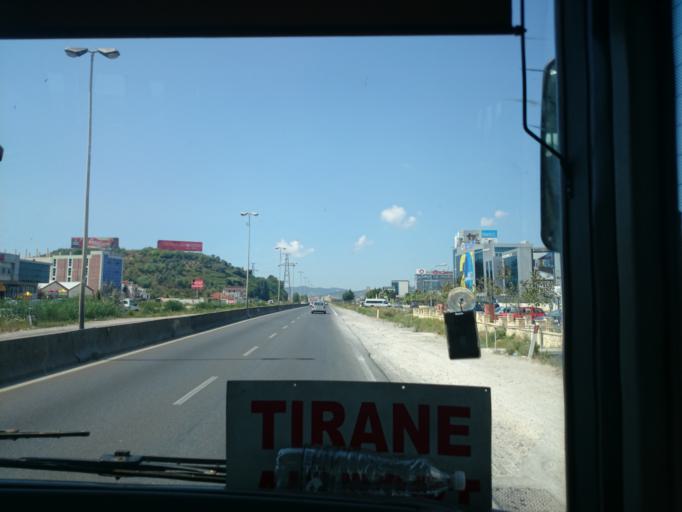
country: AL
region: Tirane
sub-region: Rrethi i Tiranes
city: Kashar
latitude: 41.3584
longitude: 19.7315
